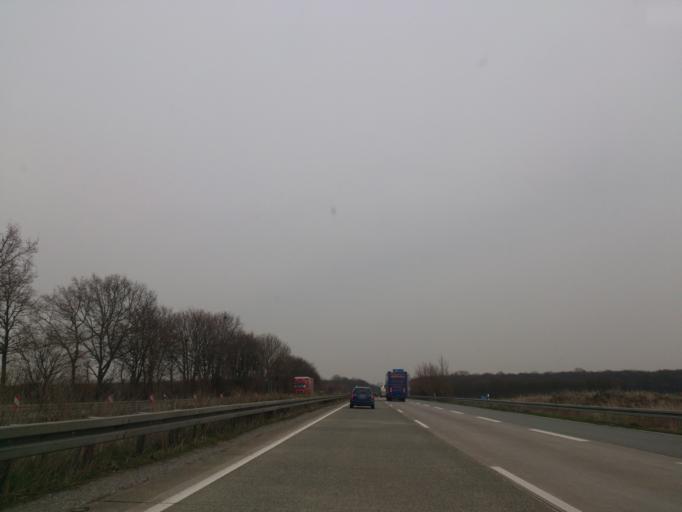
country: DE
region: North Rhine-Westphalia
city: Geseke
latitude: 51.5949
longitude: 8.4915
